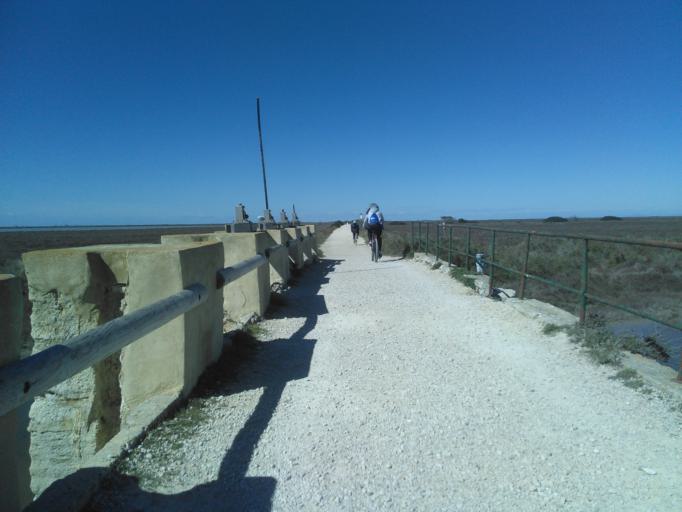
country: FR
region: Provence-Alpes-Cote d'Azur
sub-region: Departement des Bouches-du-Rhone
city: Saintes-Maries-de-la-Mer
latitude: 43.4541
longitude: 4.5837
